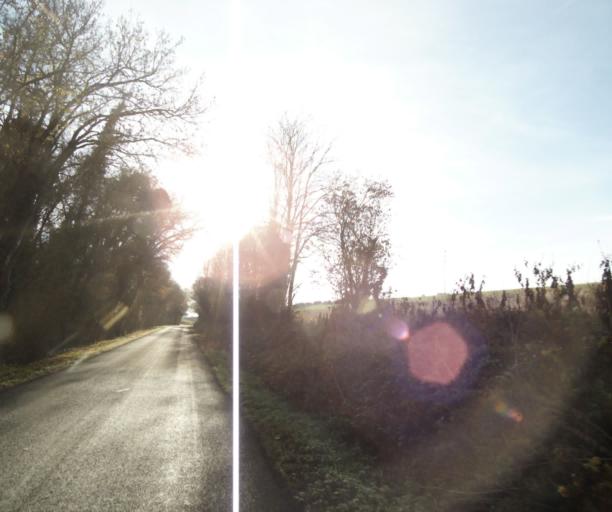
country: FR
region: Poitou-Charentes
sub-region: Departement de la Charente-Maritime
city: Chaniers
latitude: 45.7191
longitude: -0.5222
